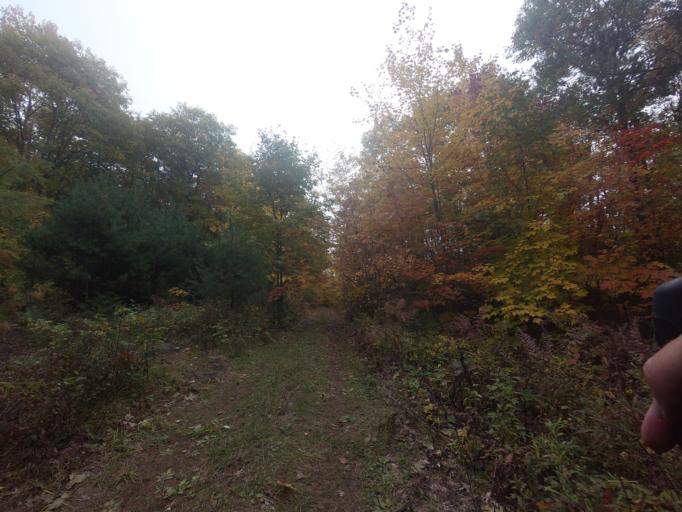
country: CA
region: Ontario
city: Pembroke
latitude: 45.7221
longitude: -77.2243
